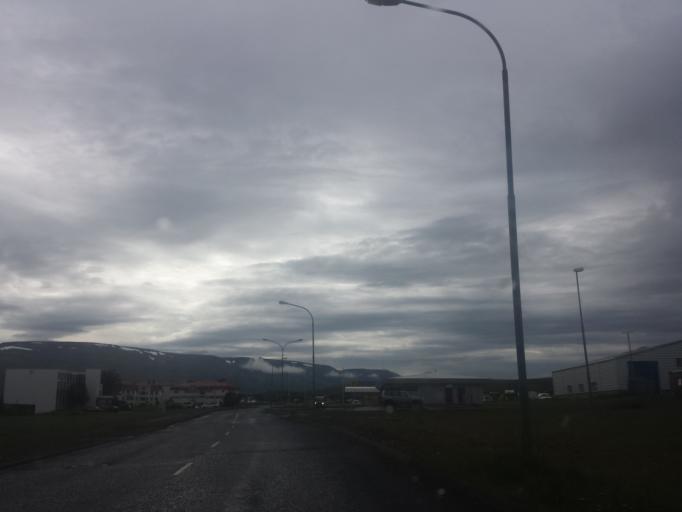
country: IS
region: Northwest
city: Saudarkrokur
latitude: 65.6570
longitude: -20.2881
